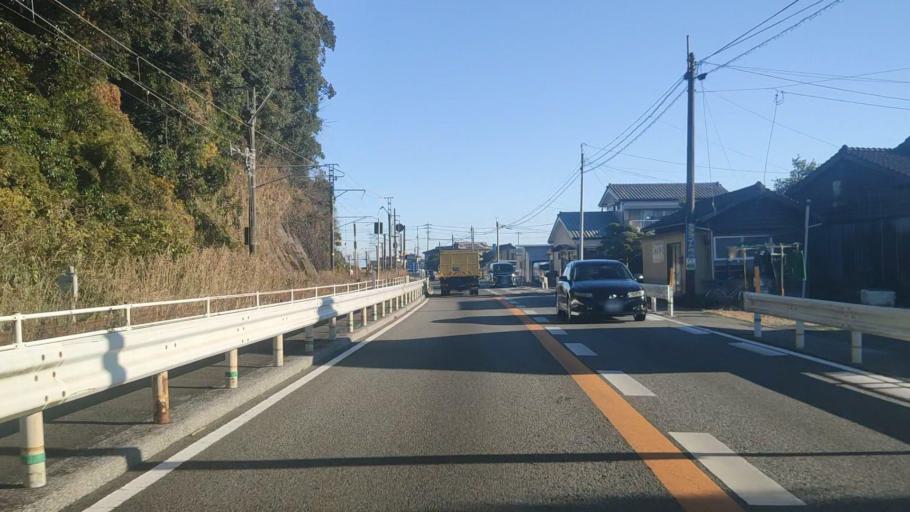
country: JP
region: Miyazaki
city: Nobeoka
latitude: 32.5105
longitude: 131.6794
